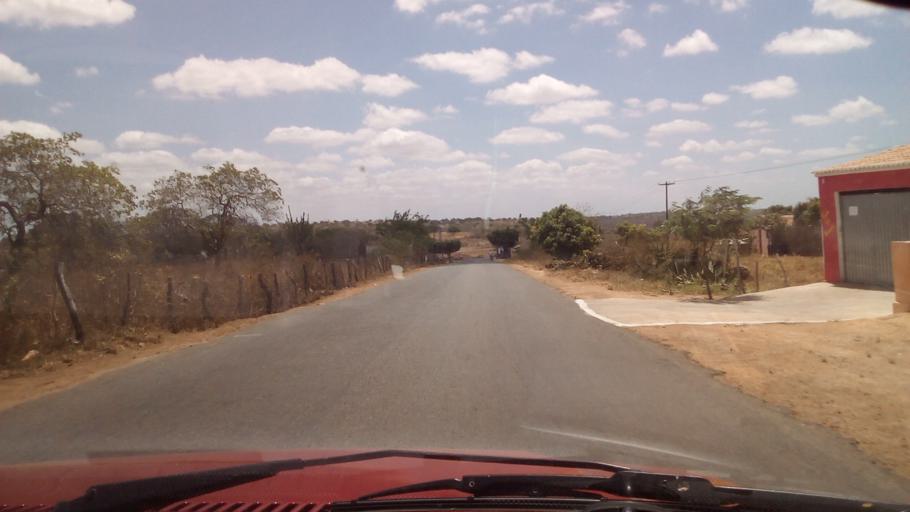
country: BR
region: Paraiba
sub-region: Cacimba De Dentro
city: Cacimba de Dentro
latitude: -6.6101
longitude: -35.8079
